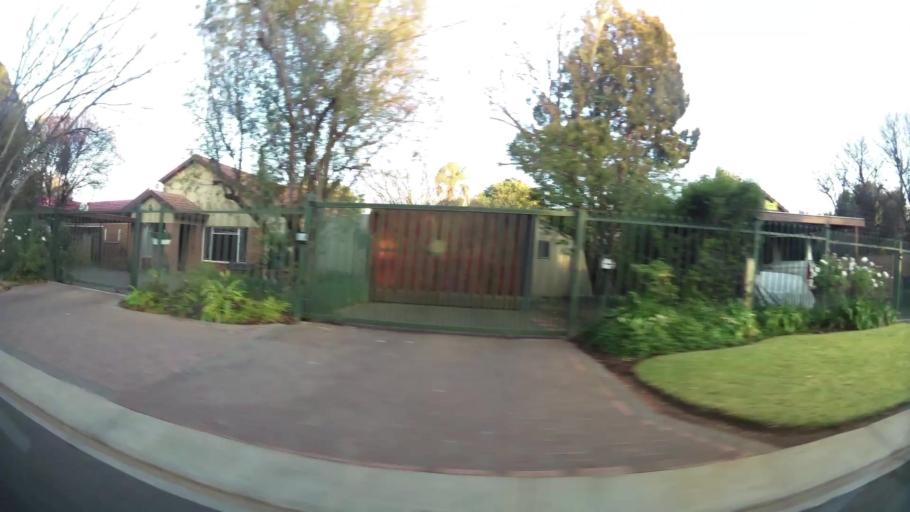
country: ZA
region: Orange Free State
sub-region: Mangaung Metropolitan Municipality
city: Bloemfontein
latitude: -29.1061
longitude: 26.1581
